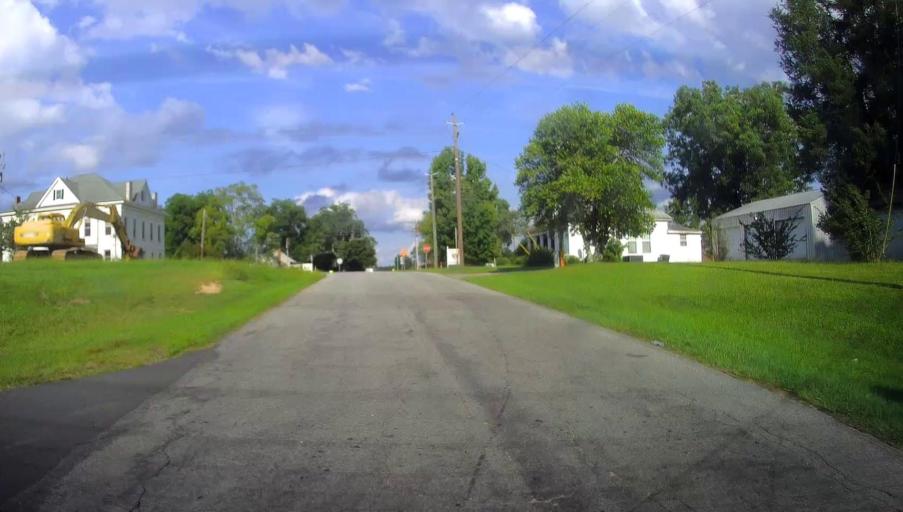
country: US
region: Georgia
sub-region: Crawford County
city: Knoxville
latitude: 32.7239
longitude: -83.9987
